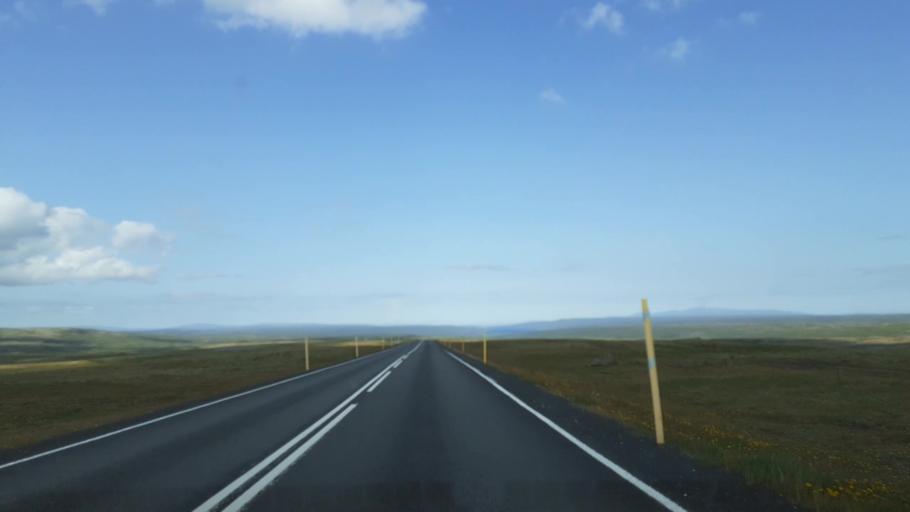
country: IS
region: West
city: Borgarnes
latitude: 65.0071
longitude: -21.0659
